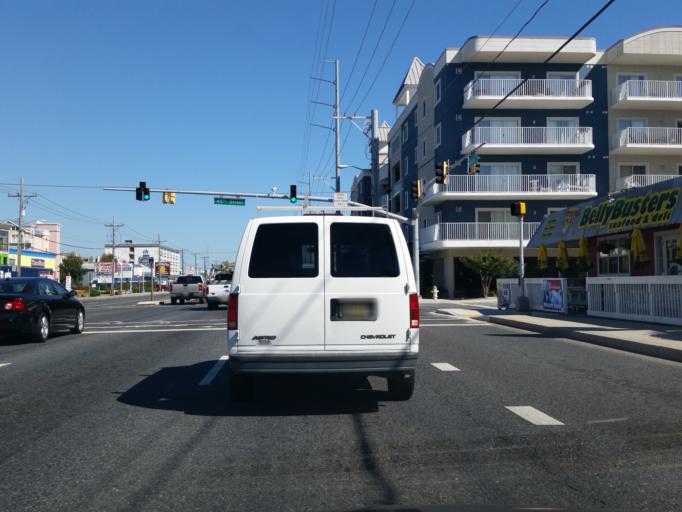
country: US
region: Maryland
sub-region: Worcester County
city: Ocean City
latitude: 38.3709
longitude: -75.0704
